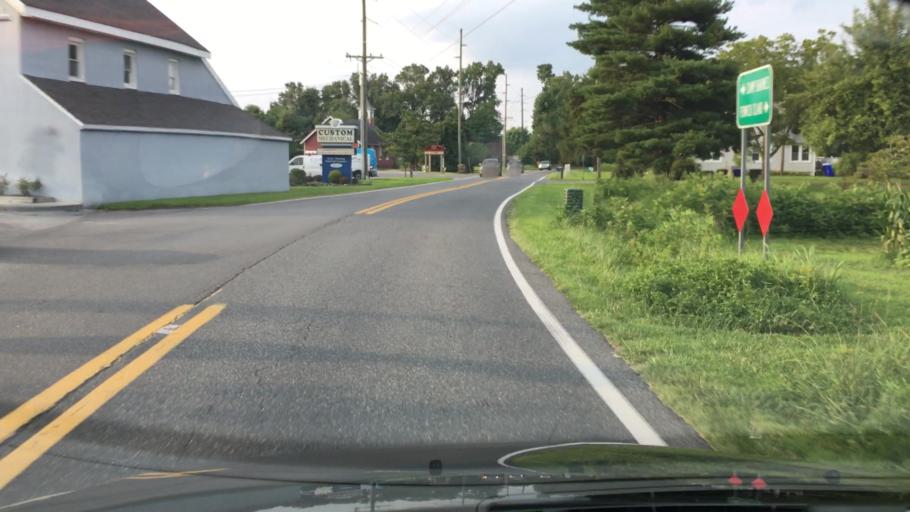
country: US
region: Delaware
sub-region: Sussex County
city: Ocean View
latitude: 38.5002
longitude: -75.1315
